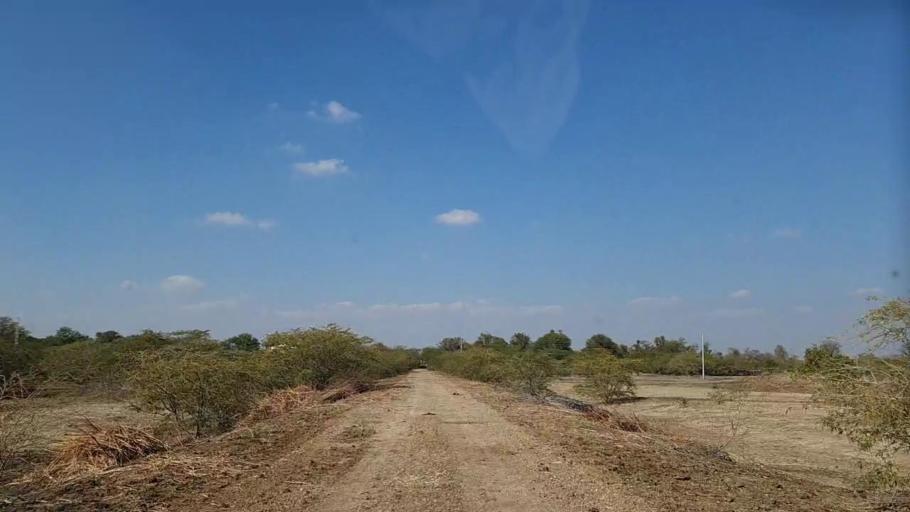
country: PK
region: Sindh
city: Pithoro
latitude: 25.6153
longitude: 69.3652
